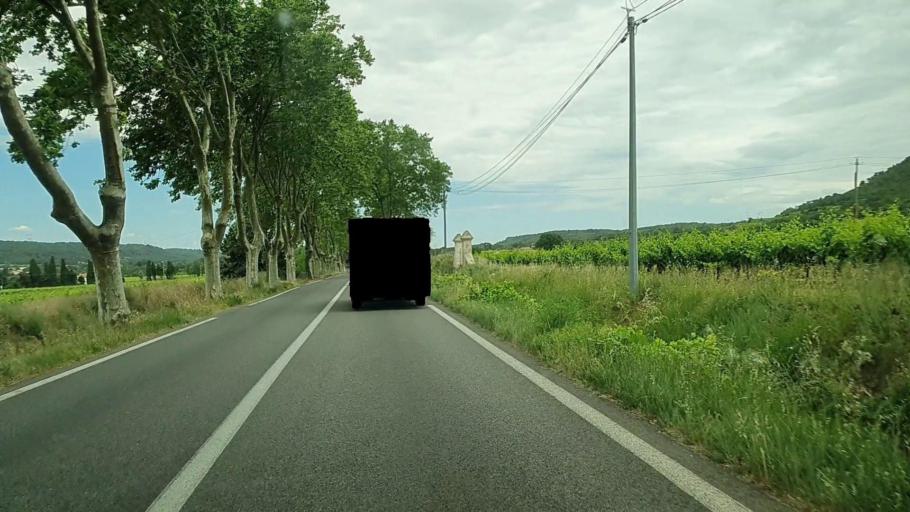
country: FR
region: Languedoc-Roussillon
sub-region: Departement du Gard
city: Tresques
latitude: 44.1171
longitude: 4.6152
